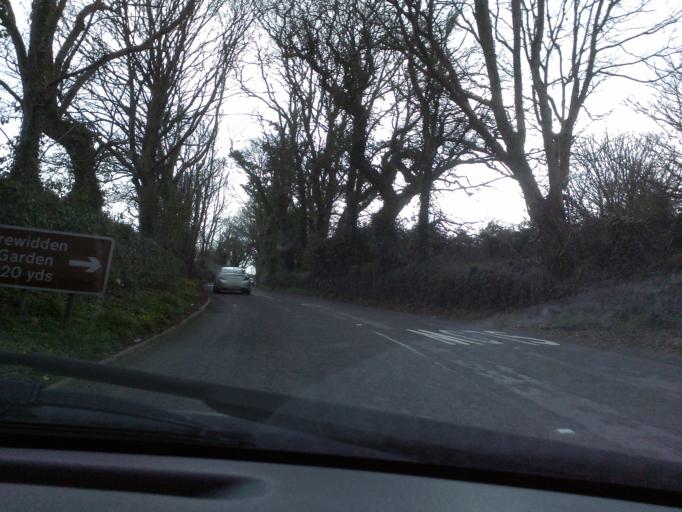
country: GB
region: England
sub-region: Cornwall
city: Penzance
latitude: 50.1092
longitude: -5.5672
